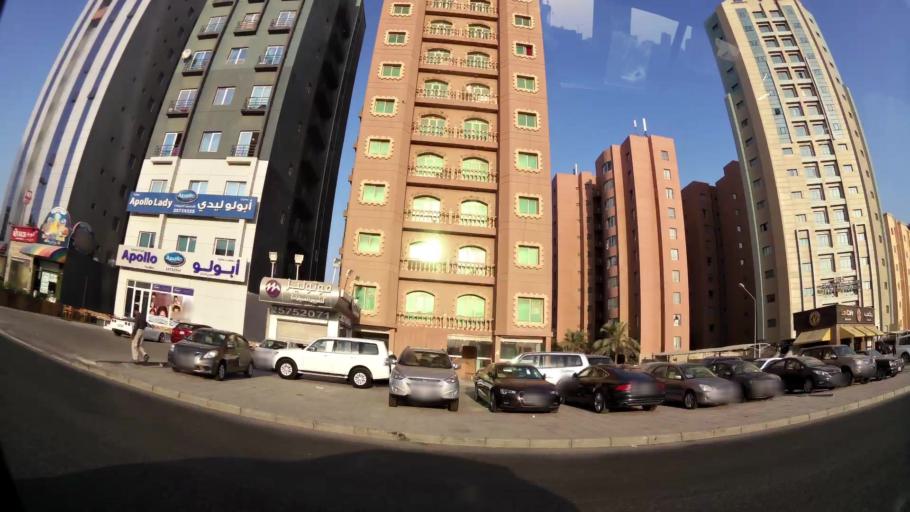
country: KW
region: Muhafazat Hawalli
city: As Salimiyah
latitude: 29.3386
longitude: 48.0703
